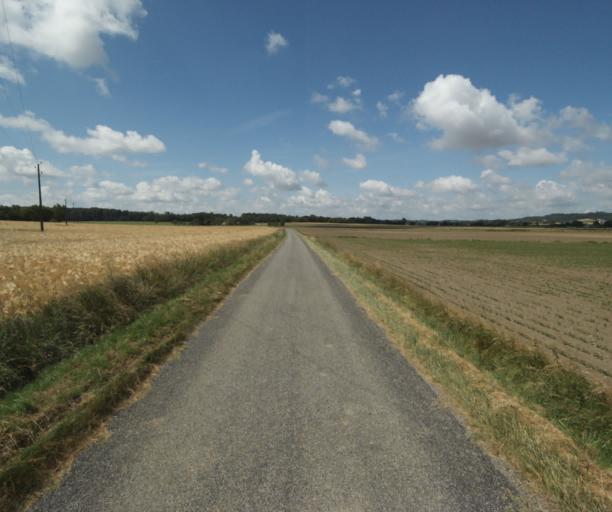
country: FR
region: Midi-Pyrenees
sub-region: Departement de la Haute-Garonne
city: Saint-Felix-Lauragais
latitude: 43.4385
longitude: 1.9246
